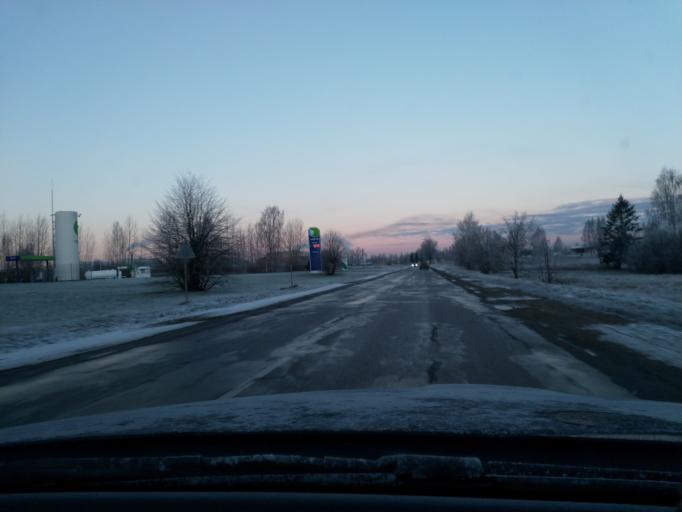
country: LV
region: Kuldigas Rajons
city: Kuldiga
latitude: 56.9532
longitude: 21.9931
